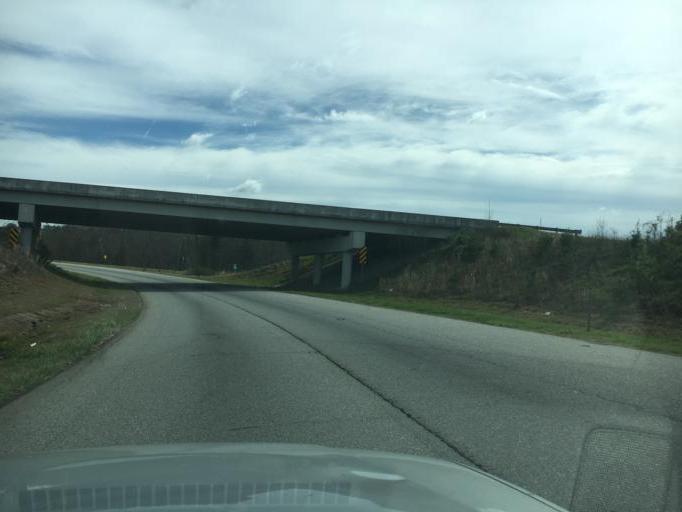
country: US
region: South Carolina
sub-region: Greenville County
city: Gantt
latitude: 34.7872
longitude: -82.4412
